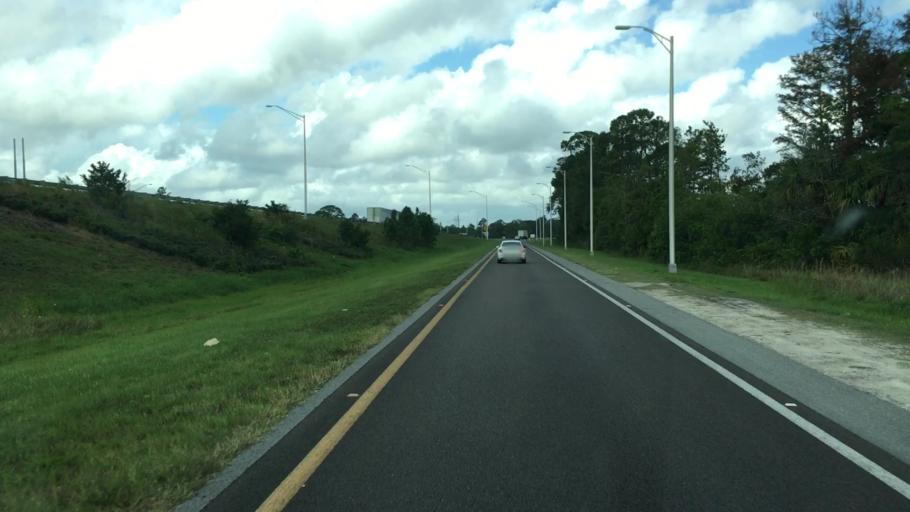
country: US
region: Florida
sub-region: Volusia County
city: Glencoe
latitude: 29.0137
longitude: -80.9876
